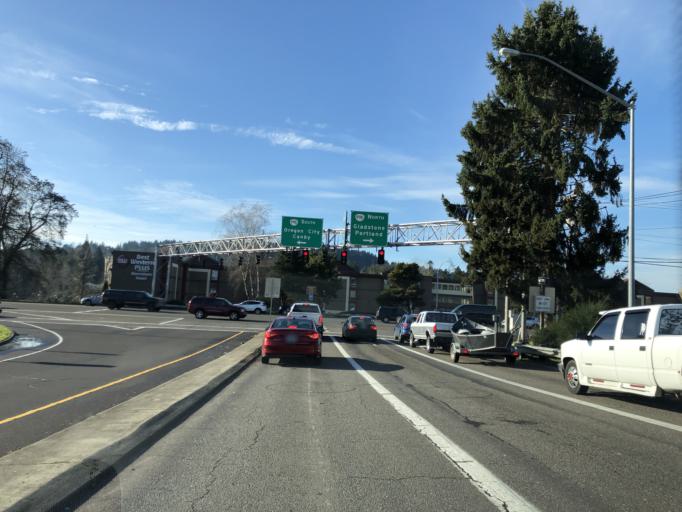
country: US
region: Oregon
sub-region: Clackamas County
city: Oregon City
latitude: 45.3668
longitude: -122.6001
